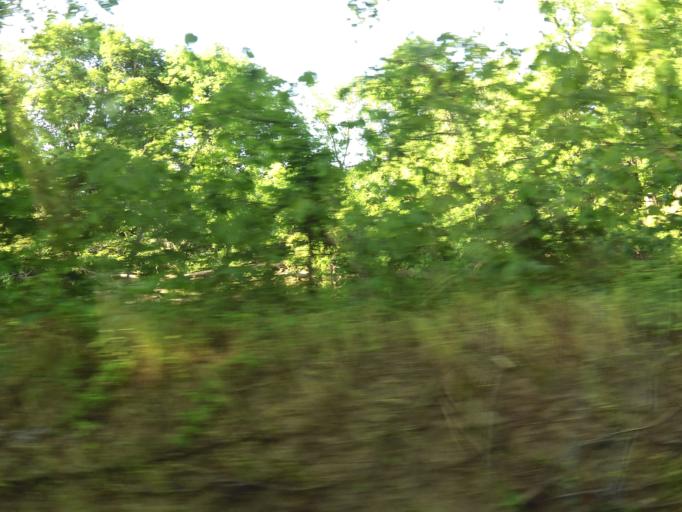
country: US
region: Tennessee
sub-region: Sevier County
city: Pigeon Forge
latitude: 35.8179
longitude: -83.5911
